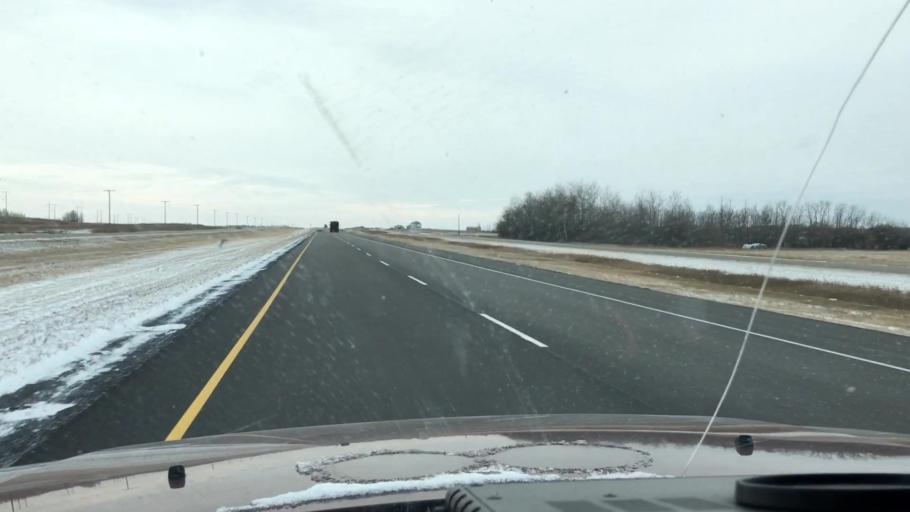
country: CA
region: Saskatchewan
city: Saskatoon
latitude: 51.9364
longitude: -106.5383
